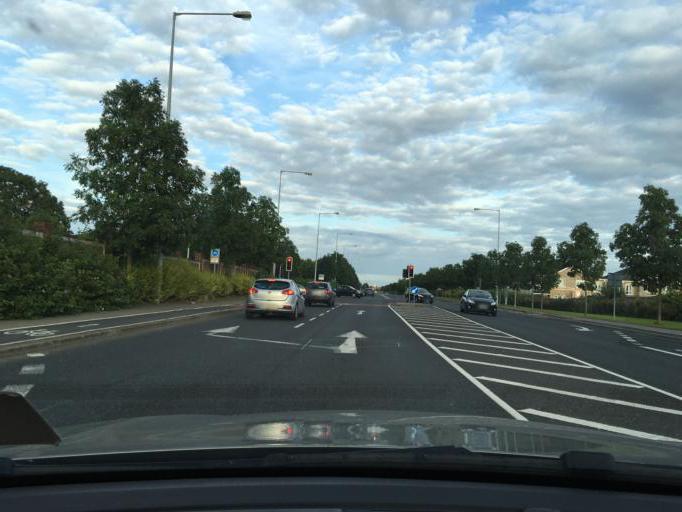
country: IE
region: Leinster
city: Hartstown
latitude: 53.3880
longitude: -6.4152
